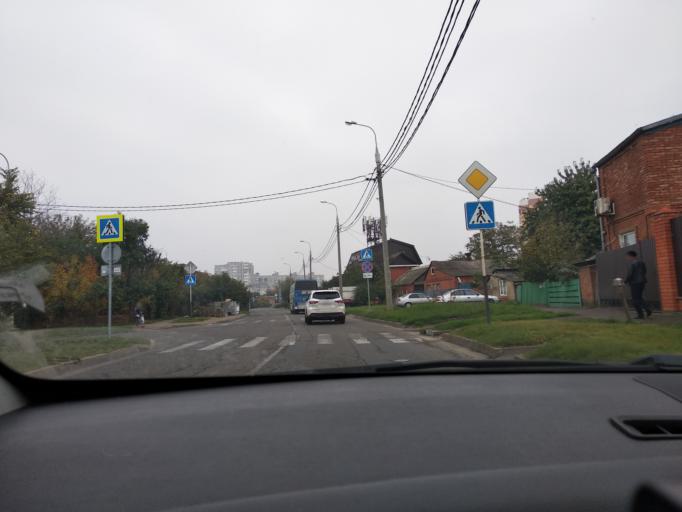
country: RU
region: Krasnodarskiy
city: Krasnodar
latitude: 45.0146
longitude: 38.9893
